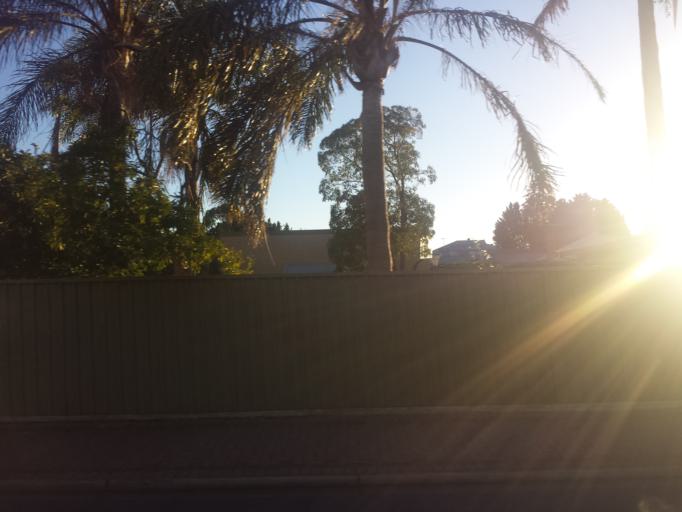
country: AU
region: South Australia
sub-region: Charles Sturt
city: Allenby Gardens
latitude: -34.8944
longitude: 138.5722
